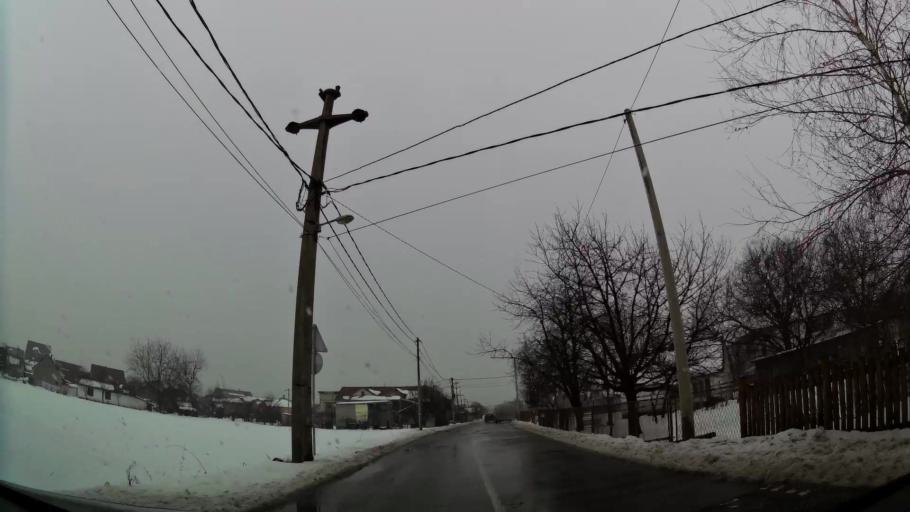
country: RS
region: Central Serbia
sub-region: Belgrade
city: Zemun
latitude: 44.8588
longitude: 20.3280
